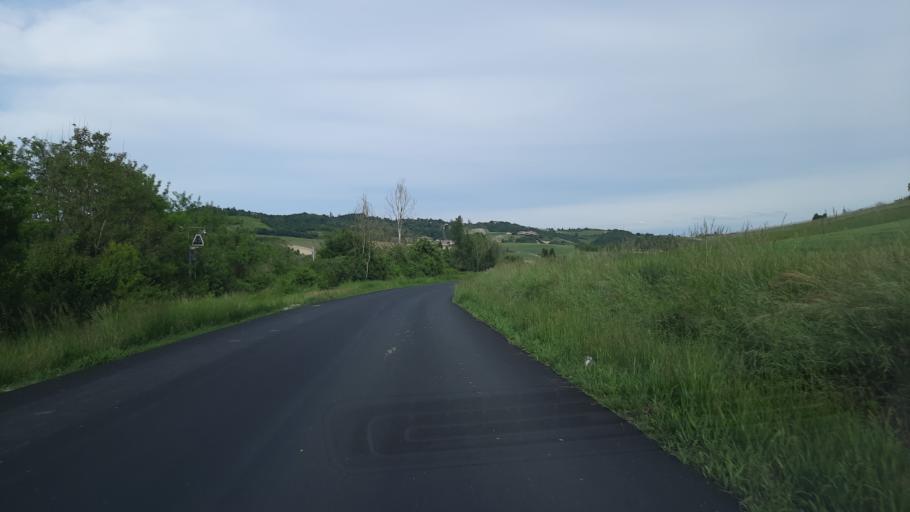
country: IT
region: Piedmont
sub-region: Provincia di Asti
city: Moncalvo
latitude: 45.0597
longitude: 8.2695
